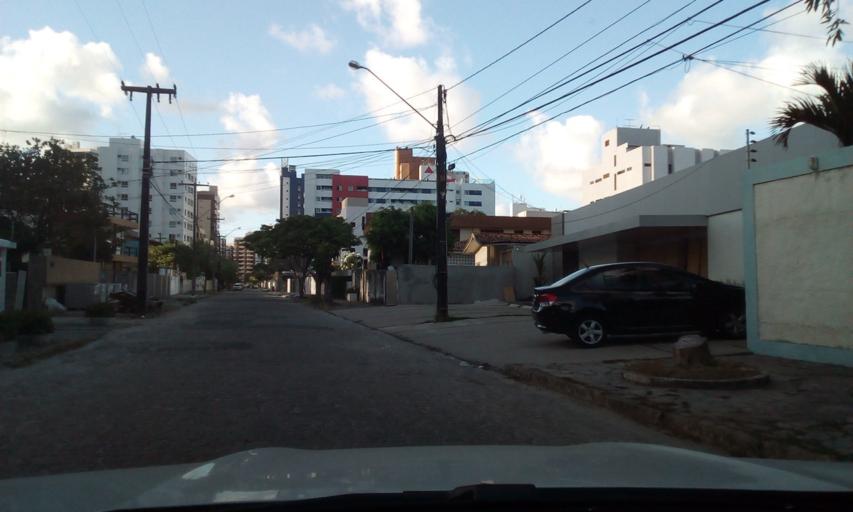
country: BR
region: Paraiba
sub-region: Joao Pessoa
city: Joao Pessoa
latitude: -7.1025
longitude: -34.8343
